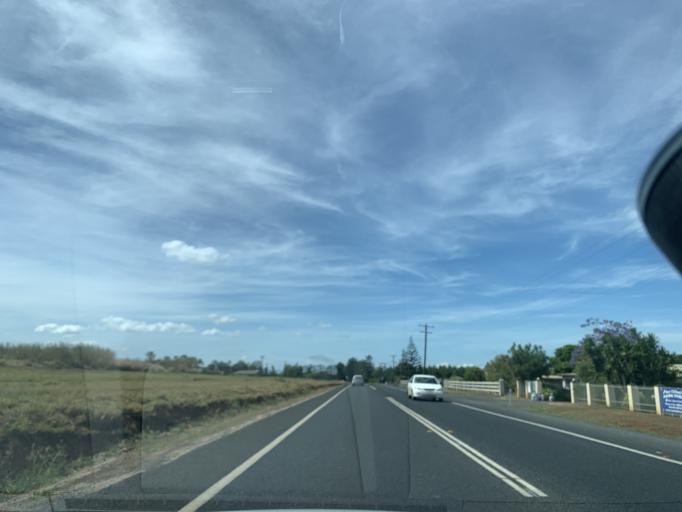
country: AU
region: Queensland
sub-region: Tablelands
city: Tolga
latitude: -17.2144
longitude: 145.4790
